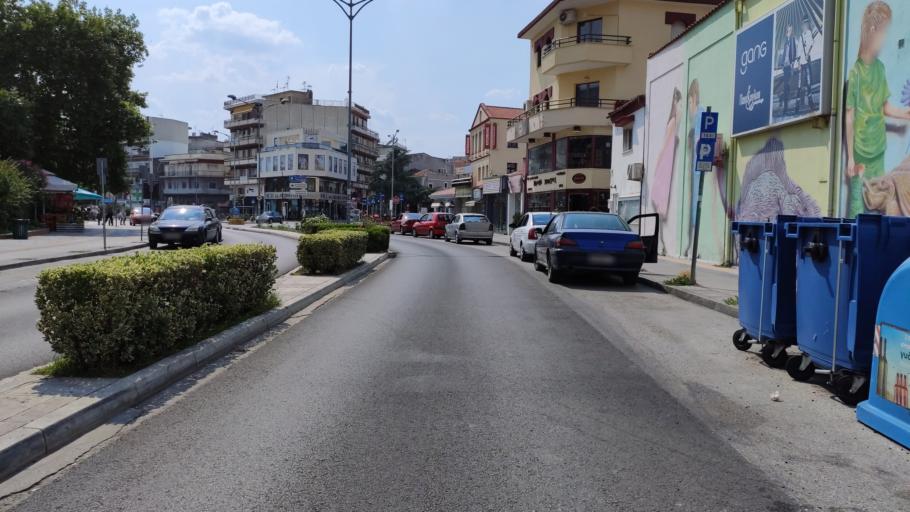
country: GR
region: East Macedonia and Thrace
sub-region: Nomos Rodopis
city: Komotini
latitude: 41.1188
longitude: 25.4036
